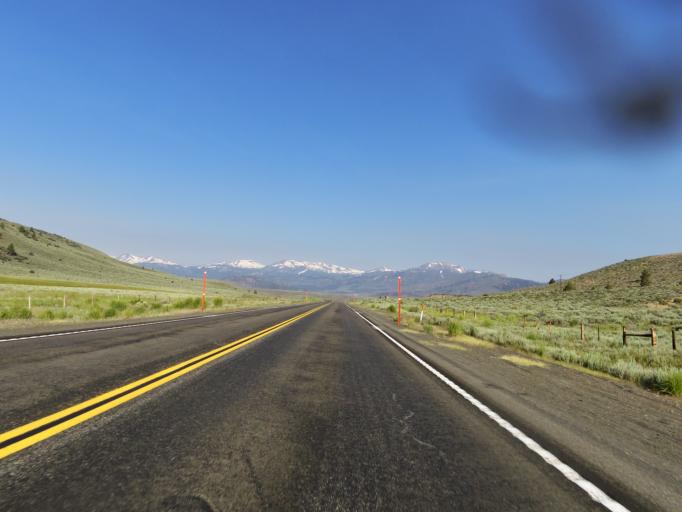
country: US
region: California
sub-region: Mono County
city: Bridgeport
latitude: 38.3499
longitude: -119.3890
